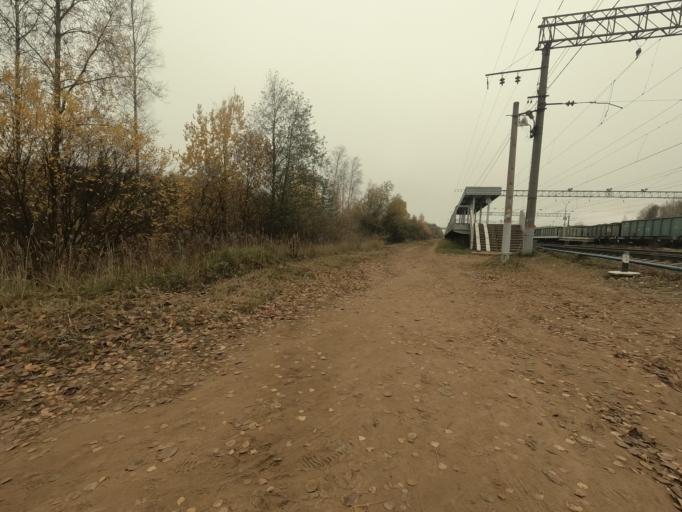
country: RU
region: Leningrad
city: Pavlovo
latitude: 59.7670
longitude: 30.9501
